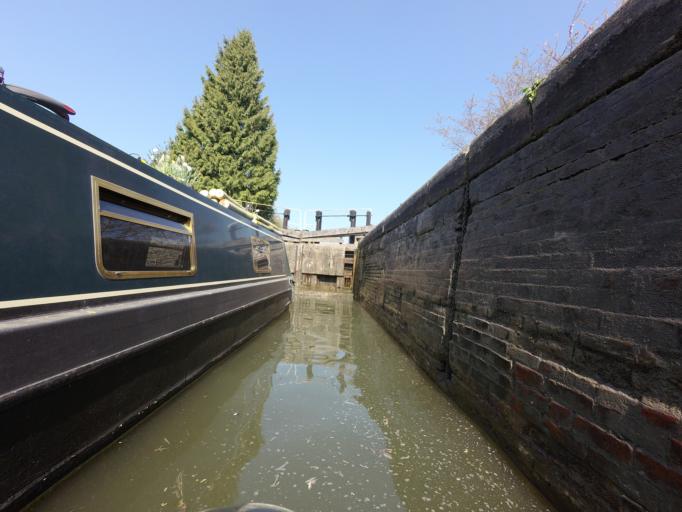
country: GB
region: England
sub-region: Hertfordshire
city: Berkhamsted
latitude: 51.7604
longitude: -0.5573
